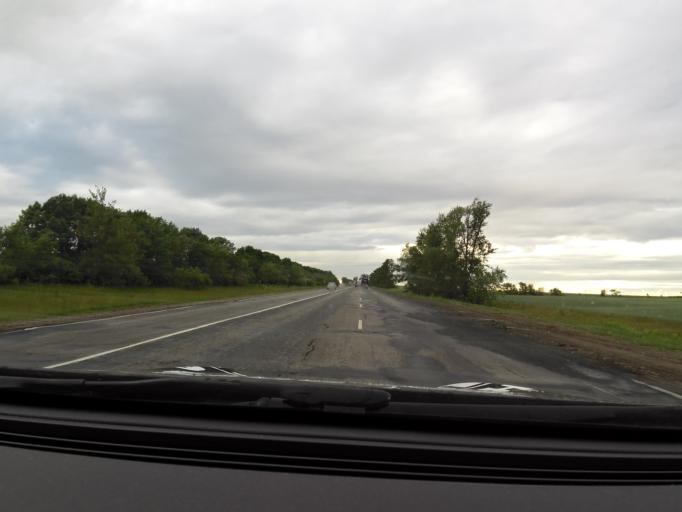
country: RU
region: Chuvashia
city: Tsivil'sk
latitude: 55.7915
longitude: 47.6733
